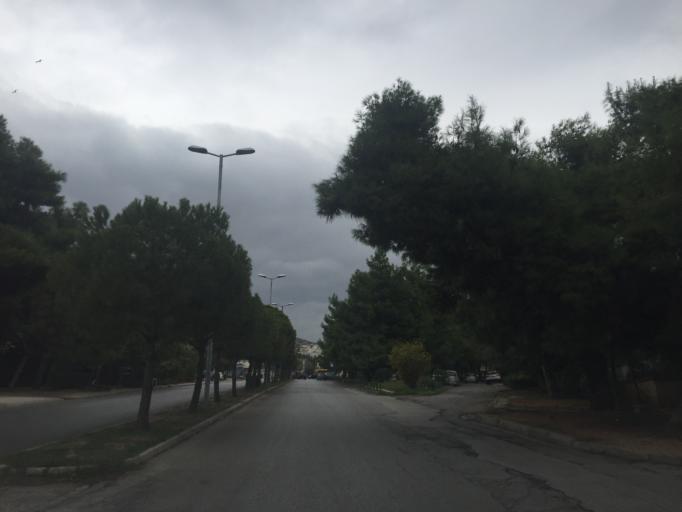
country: GR
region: Attica
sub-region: Nomarchia Athinas
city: Glyfada
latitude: 37.8537
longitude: 23.7634
